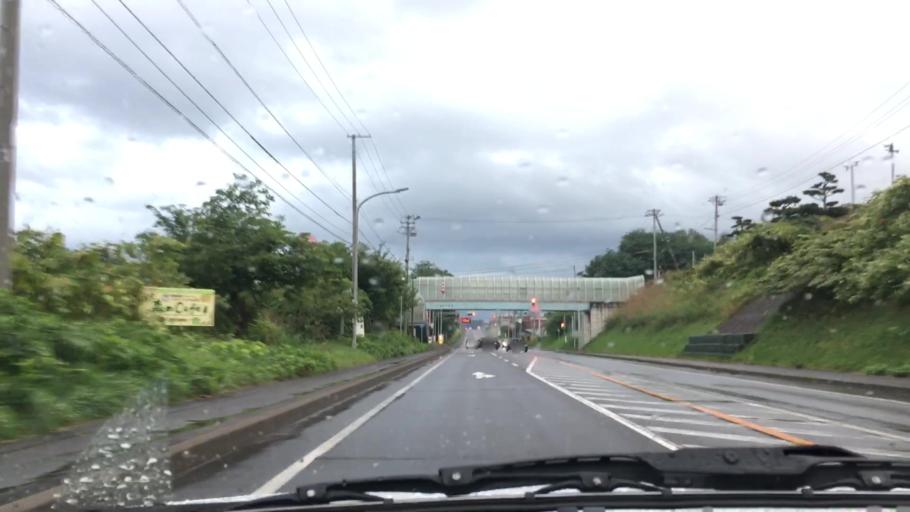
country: JP
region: Hokkaido
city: Nanae
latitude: 42.0976
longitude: 140.5699
